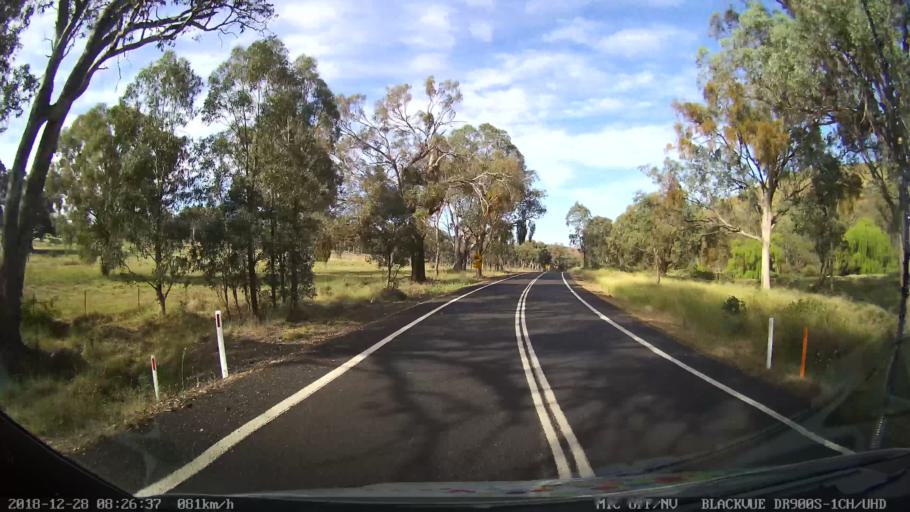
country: AU
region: New South Wales
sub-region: Blayney
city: Blayney
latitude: -33.9378
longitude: 149.3458
